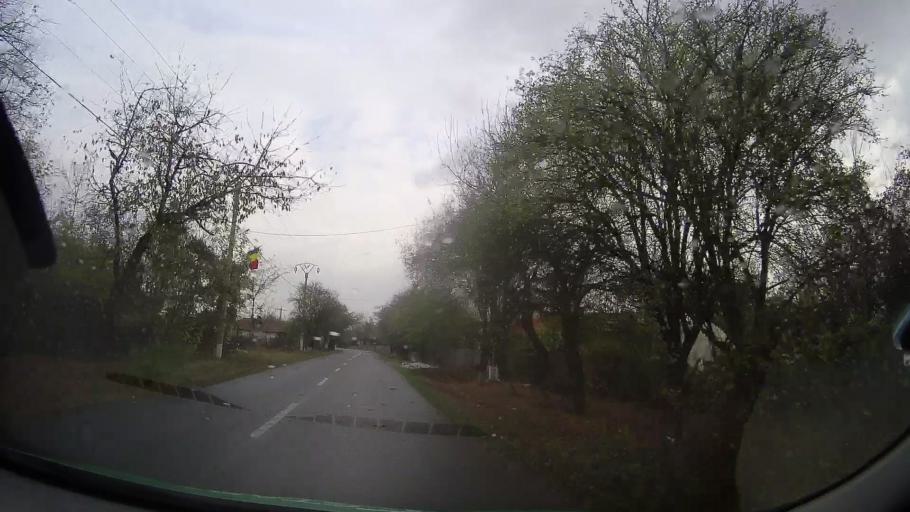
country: RO
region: Ialomita
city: Brazii
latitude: 44.7802
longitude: 26.3284
